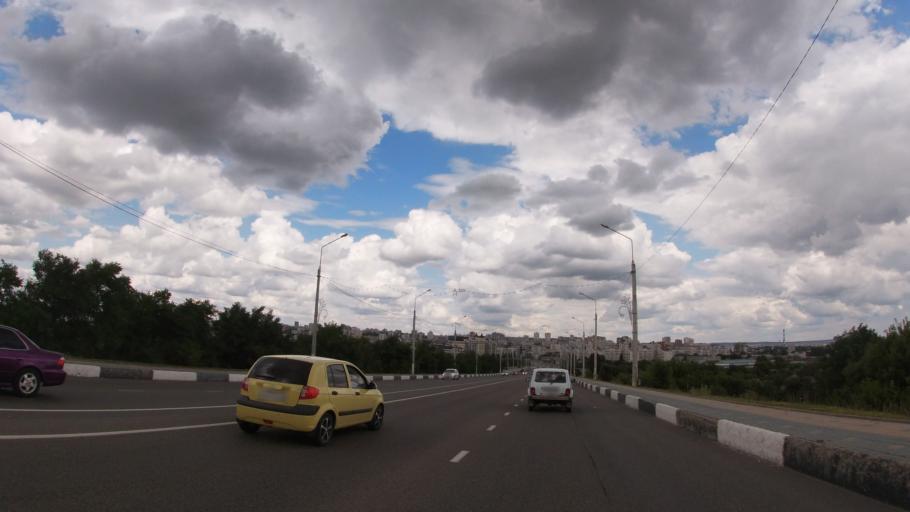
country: RU
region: Belgorod
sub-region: Belgorodskiy Rayon
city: Belgorod
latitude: 50.5837
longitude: 36.5853
